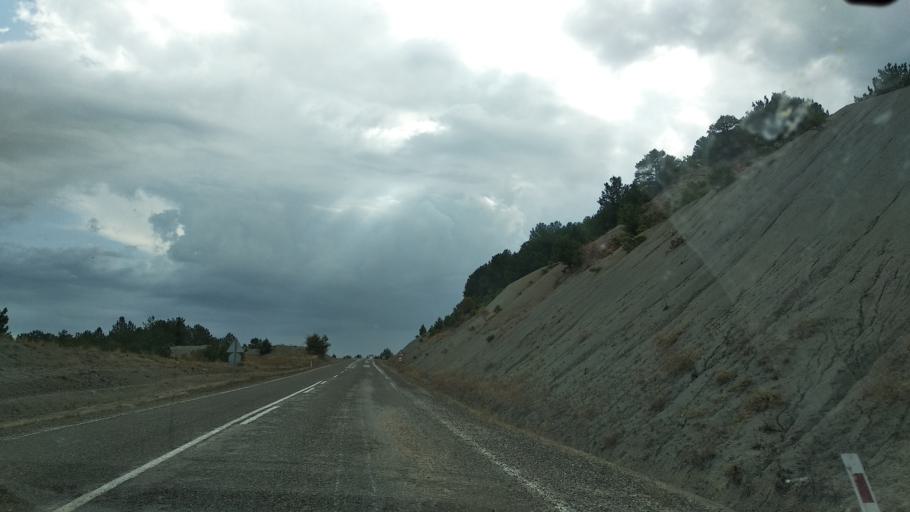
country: TR
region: Bolu
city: Seben
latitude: 40.3572
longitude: 31.4813
